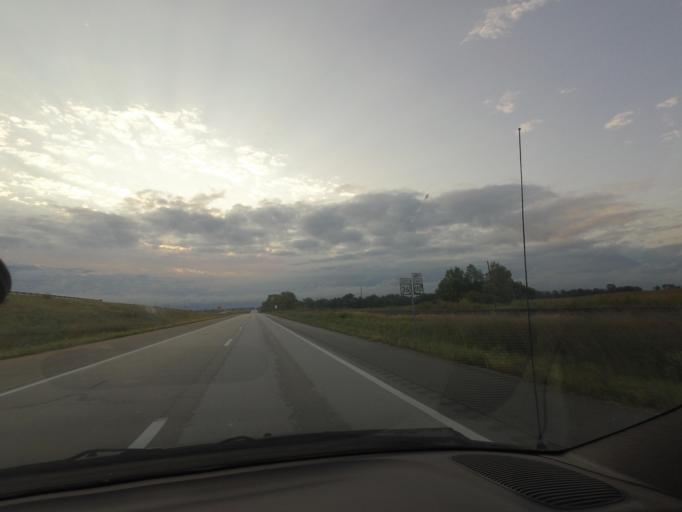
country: US
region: Missouri
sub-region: Shelby County
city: Shelbina
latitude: 39.7045
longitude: -92.0861
